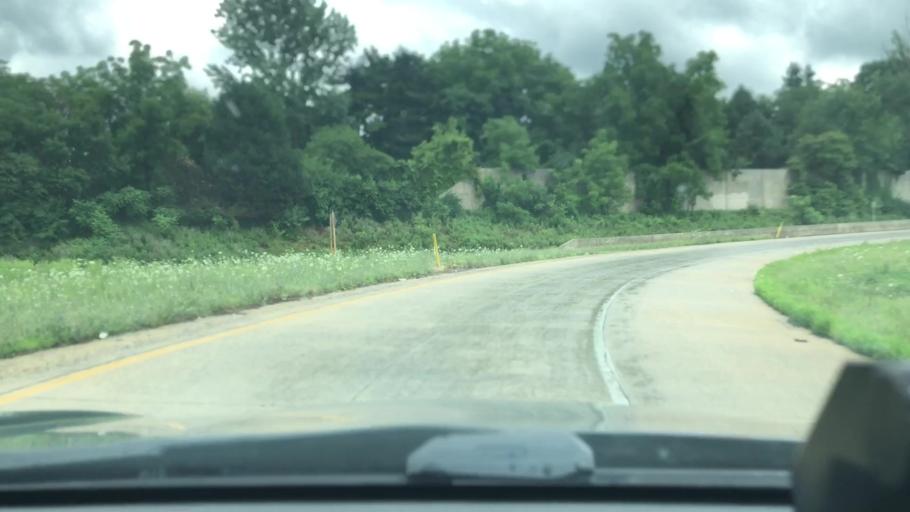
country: US
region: Pennsylvania
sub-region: Lehigh County
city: Wescosville
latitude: 40.5728
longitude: -75.5371
